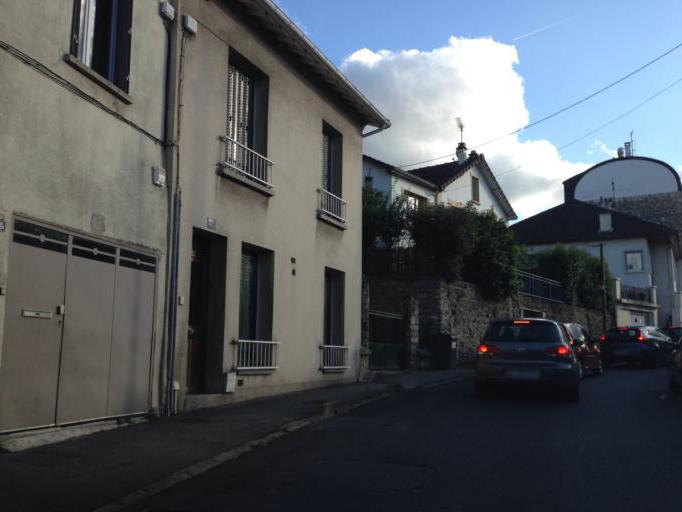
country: FR
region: Ile-de-France
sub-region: Departement des Hauts-de-Seine
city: Meudon
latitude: 48.8120
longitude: 2.2490
